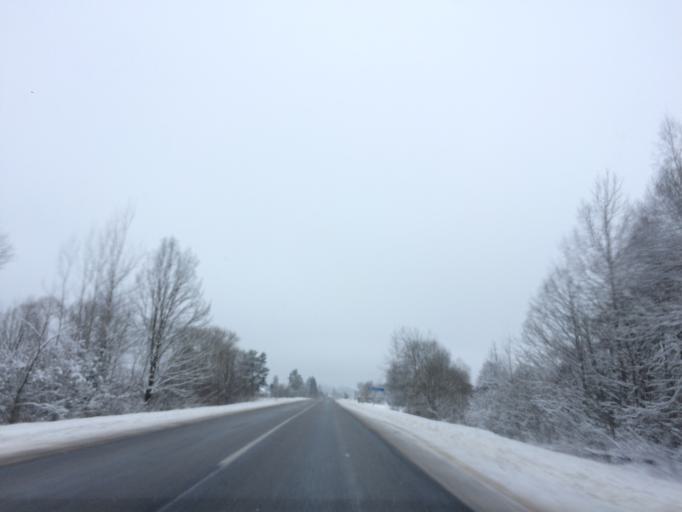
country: LV
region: Rezekne
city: Rezekne
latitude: 56.6170
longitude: 27.4504
